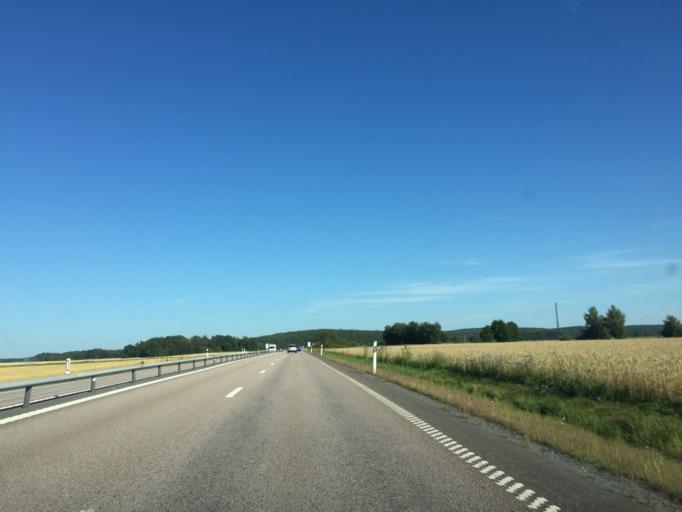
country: SE
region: Vaestmanland
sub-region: Arboga Kommun
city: Arboga
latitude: 59.3974
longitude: 15.9010
